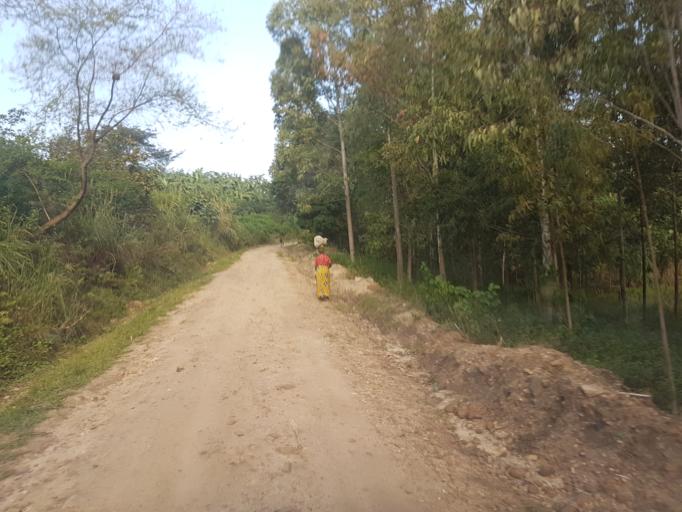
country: UG
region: Western Region
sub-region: Mitoma District
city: Mitoma
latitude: -0.6799
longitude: 29.9068
